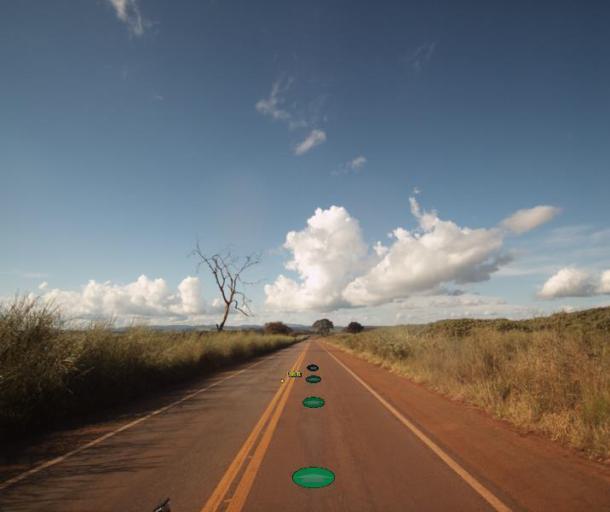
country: BR
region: Goias
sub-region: Itaberai
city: Itaberai
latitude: -16.0240
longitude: -49.7767
